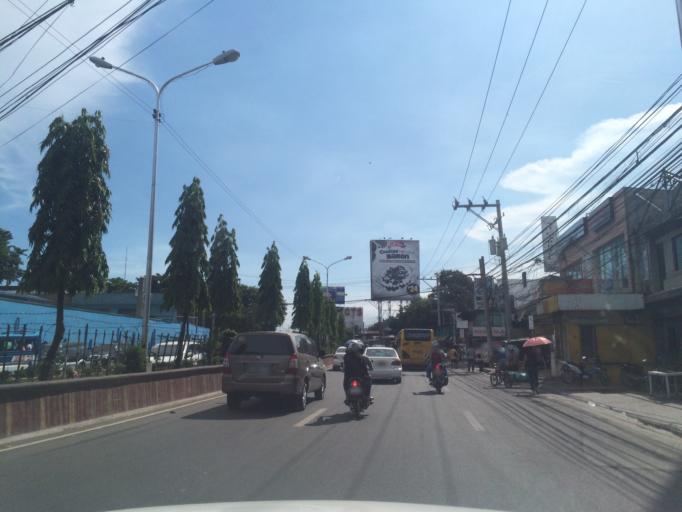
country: PH
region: Central Visayas
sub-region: Cebu City
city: Calero
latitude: 10.2986
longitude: 123.8932
